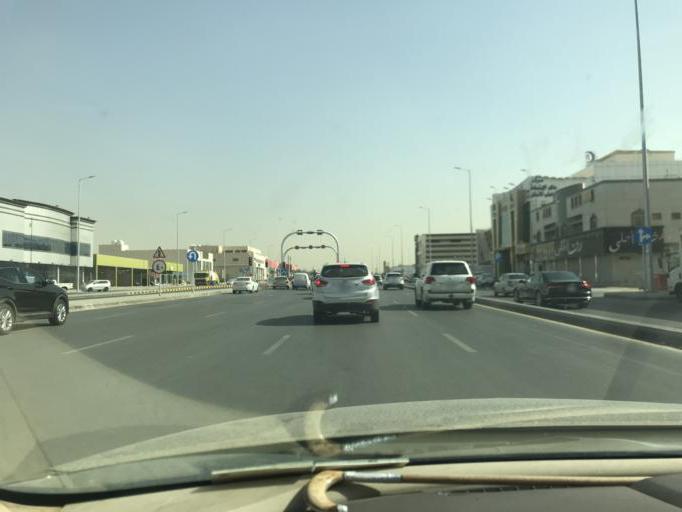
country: SA
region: Ar Riyad
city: Riyadh
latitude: 24.7868
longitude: 46.7469
